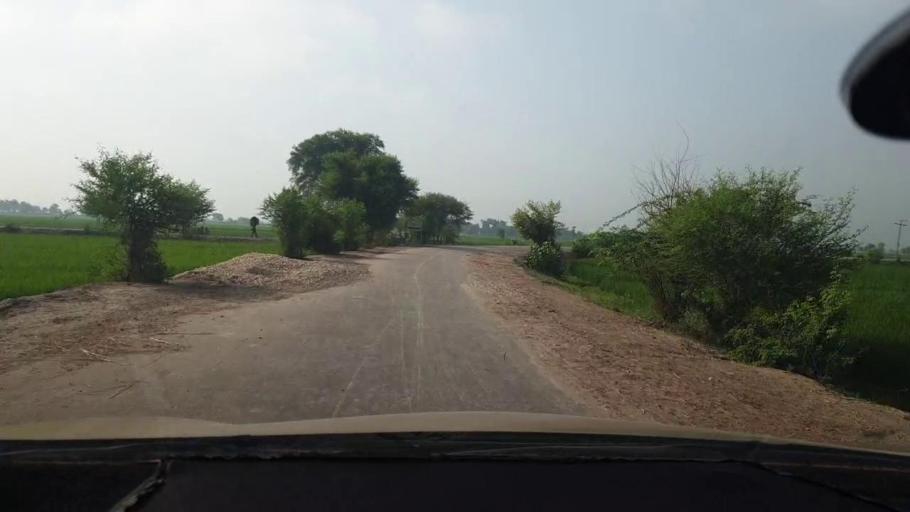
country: PK
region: Sindh
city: Goth Garelo
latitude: 27.4807
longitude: 68.0151
